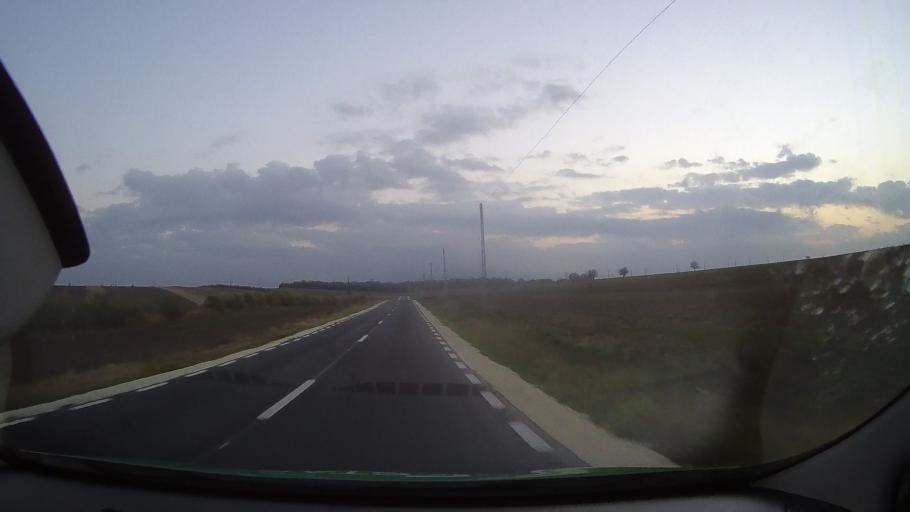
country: RO
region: Constanta
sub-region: Comuna Oltina
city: Oltina
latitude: 44.1190
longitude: 27.6666
